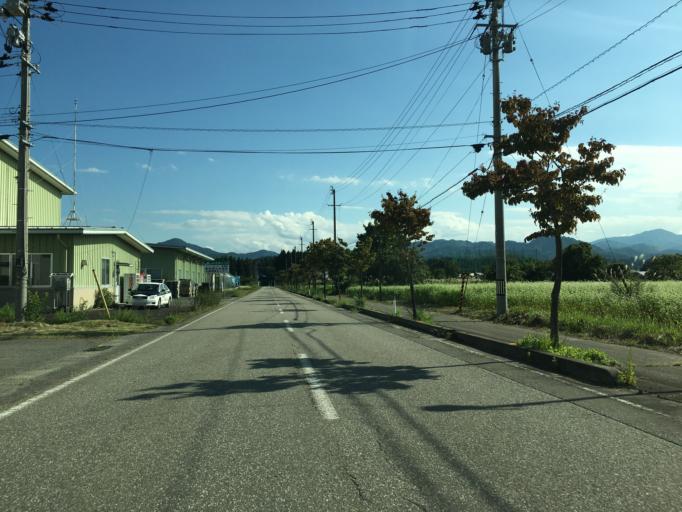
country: JP
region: Fukushima
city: Kitakata
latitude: 37.5995
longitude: 139.6526
